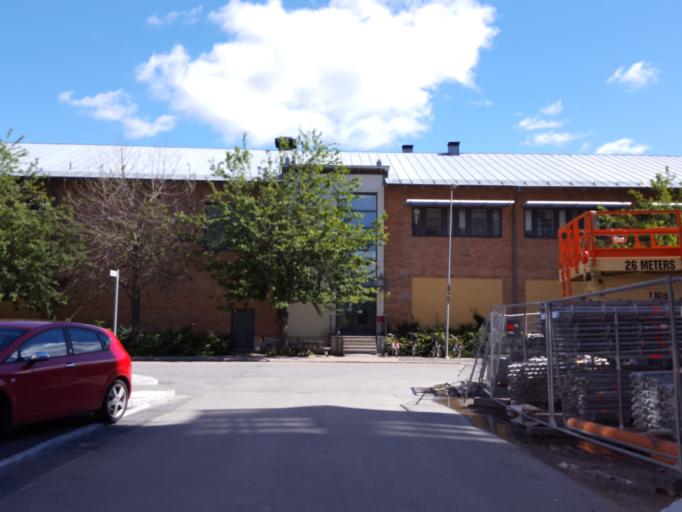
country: SE
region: Uppsala
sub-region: Uppsala Kommun
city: Uppsala
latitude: 59.8497
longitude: 17.6570
